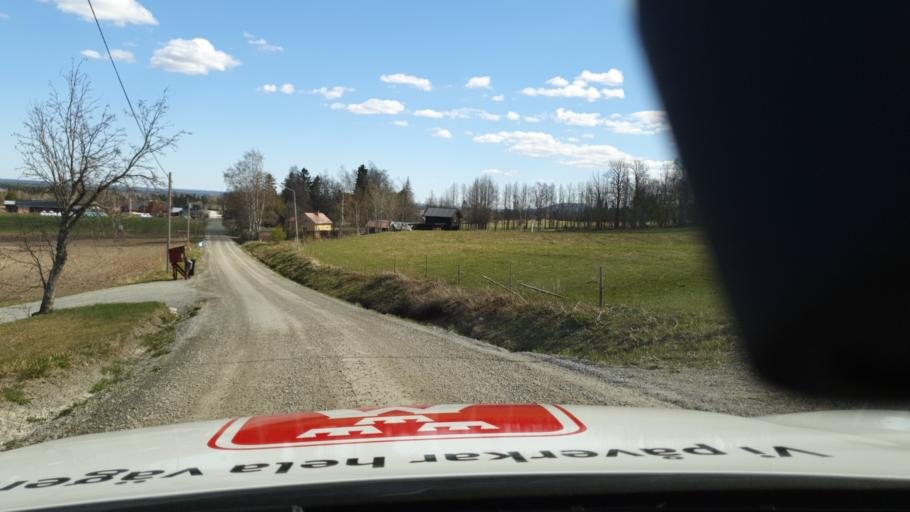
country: SE
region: Jaemtland
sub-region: Bergs Kommun
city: Hoverberg
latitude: 62.9189
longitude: 14.3063
